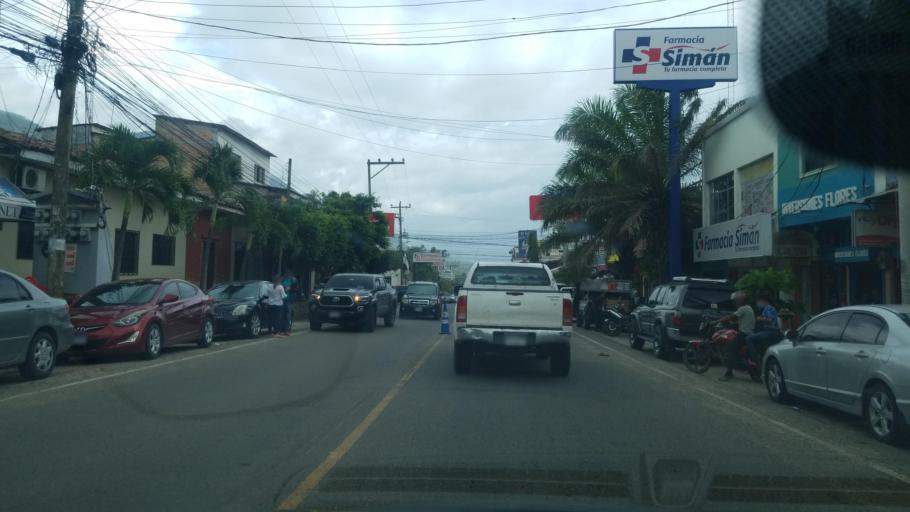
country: HN
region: Ocotepeque
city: Nueva Ocotepeque
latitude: 14.4370
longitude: -89.1829
